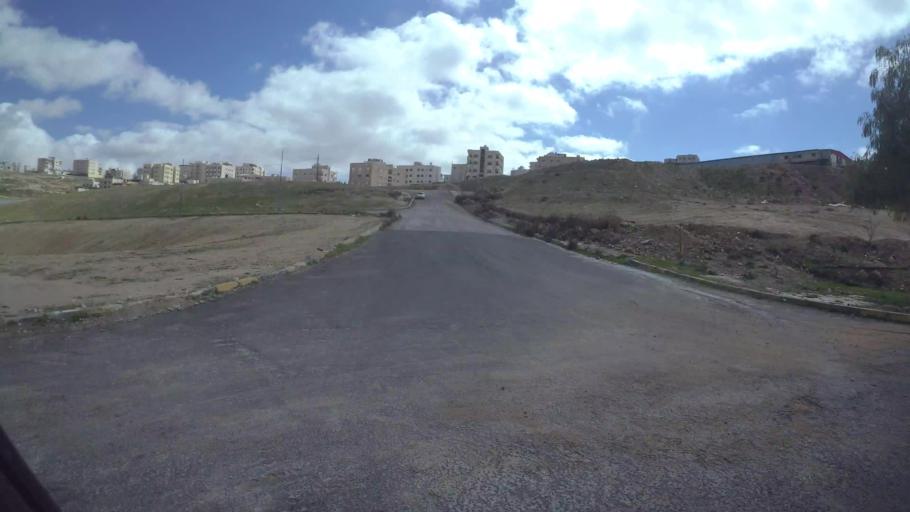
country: JO
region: Amman
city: Al Jubayhah
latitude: 32.0637
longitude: 35.8853
